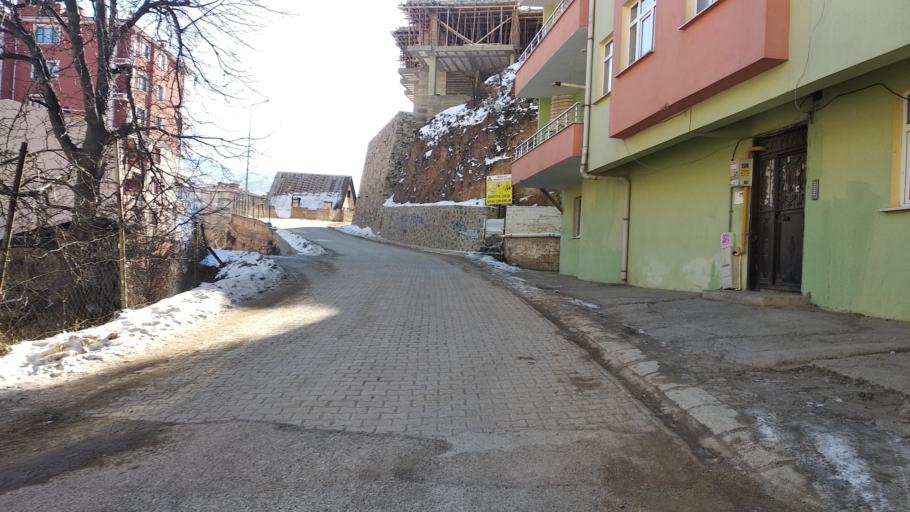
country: TR
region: Gumushane
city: Gumushkhane
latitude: 40.4568
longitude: 39.4863
